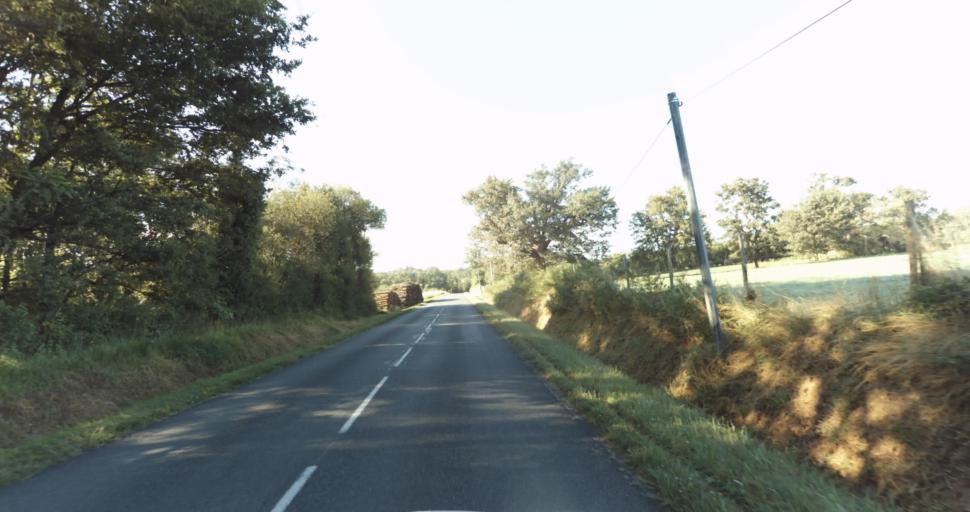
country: FR
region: Aquitaine
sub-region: Departement de la Gironde
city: Bazas
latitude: 44.4078
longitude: -0.2071
